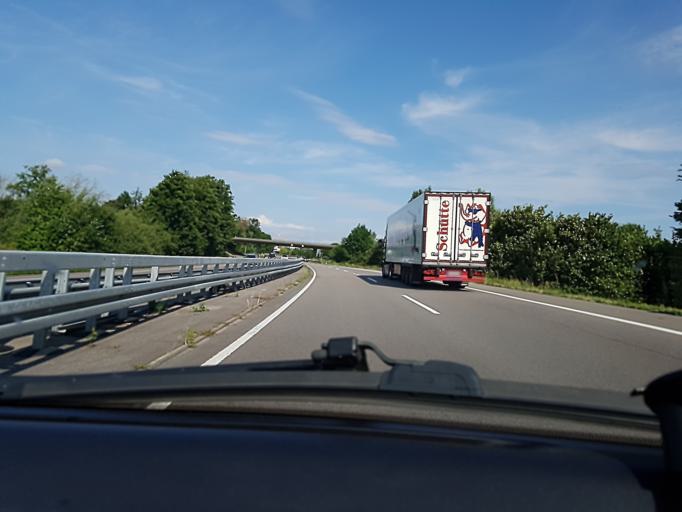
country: DE
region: Baden-Wuerttemberg
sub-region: Freiburg Region
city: Willstatt
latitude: 48.5386
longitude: 7.9119
